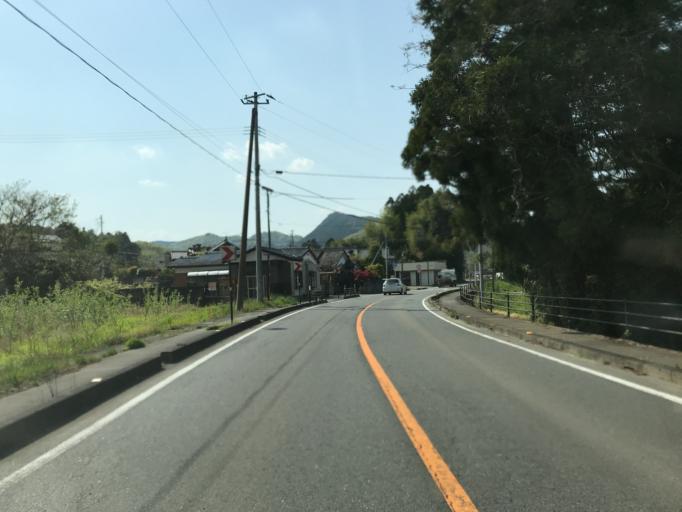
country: JP
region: Fukushima
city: Iwaki
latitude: 36.9531
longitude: 140.7602
